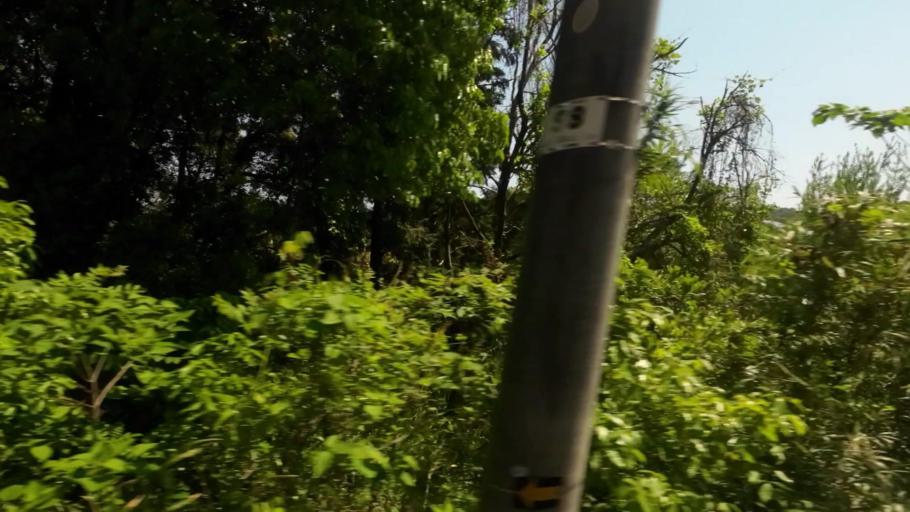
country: JP
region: Ehime
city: Niihama
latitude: 33.9687
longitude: 133.3577
